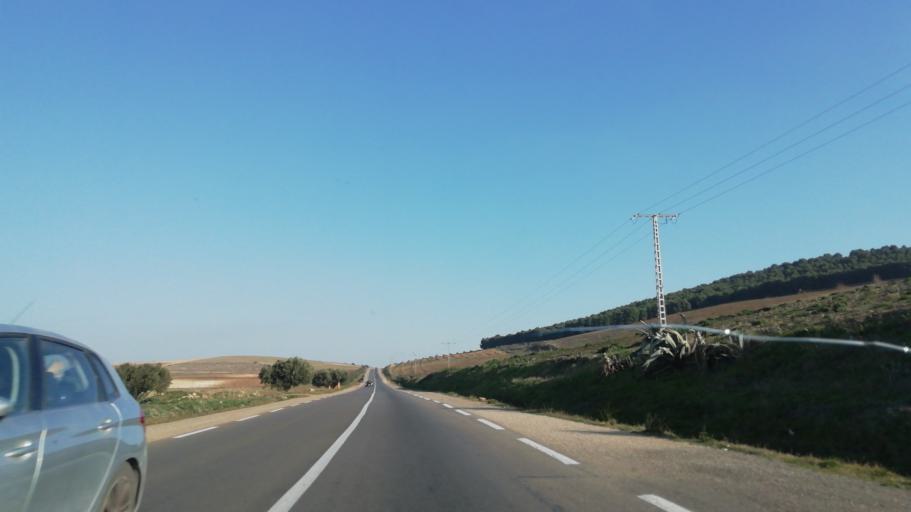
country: DZ
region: Ain Temouchent
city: Hammam Bou Hadjar
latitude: 35.1657
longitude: -0.8859
